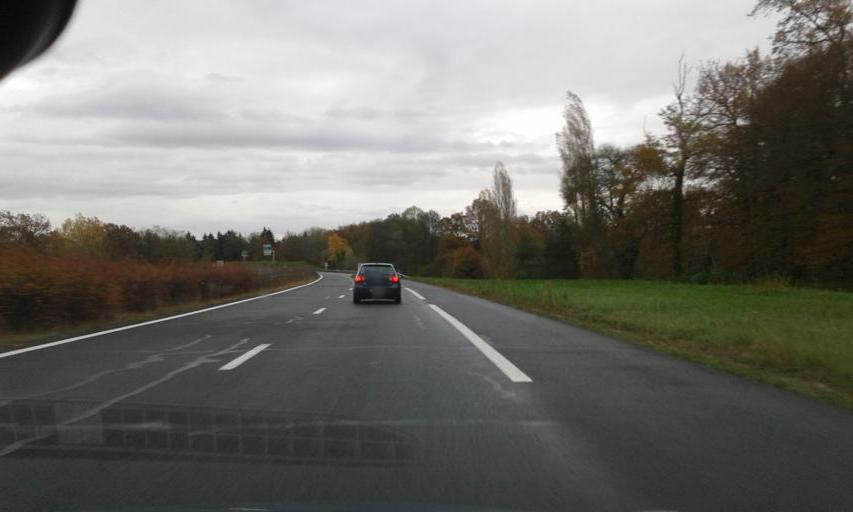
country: FR
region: Centre
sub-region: Departement du Loiret
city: Chateauneuf-sur-Loire
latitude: 47.8836
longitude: 2.2261
